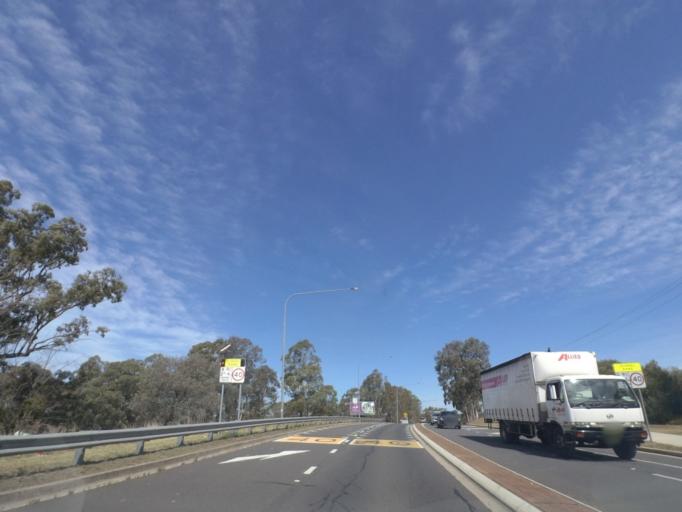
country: AU
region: New South Wales
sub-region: Campbelltown Municipality
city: Campbelltown
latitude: -34.0465
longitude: 150.8020
